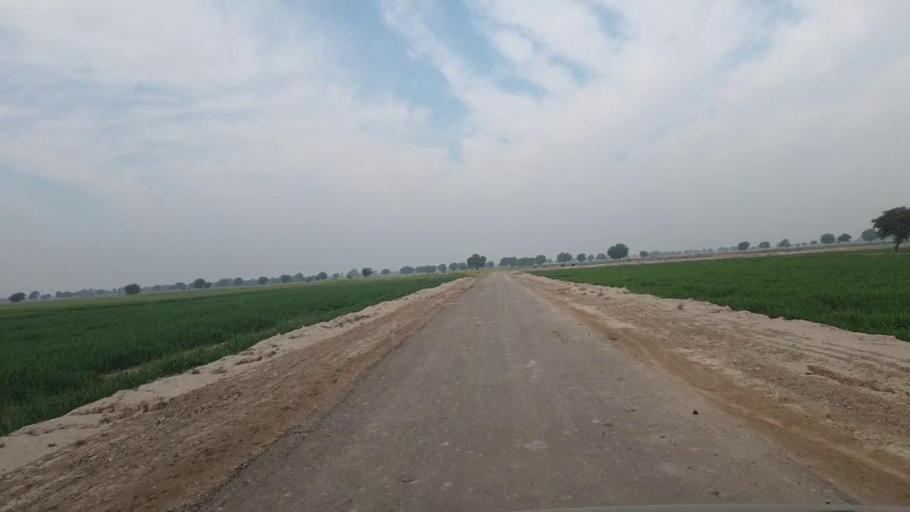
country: PK
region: Sindh
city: Shahdadpur
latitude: 25.9510
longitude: 68.6717
